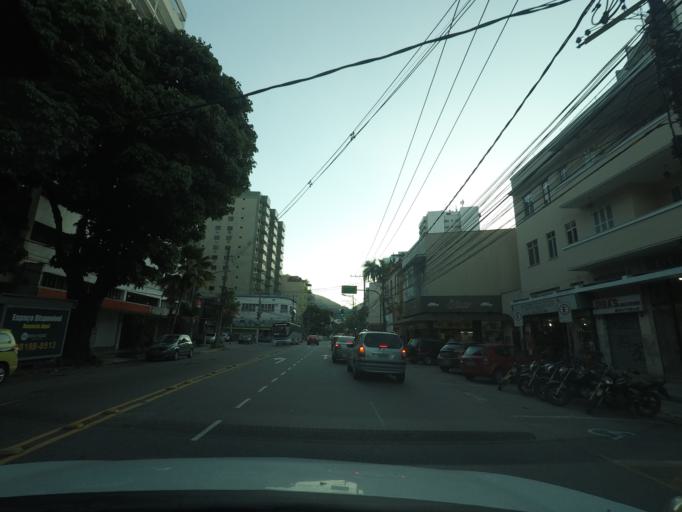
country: BR
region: Rio de Janeiro
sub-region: Rio De Janeiro
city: Rio de Janeiro
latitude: -22.9349
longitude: -43.2433
